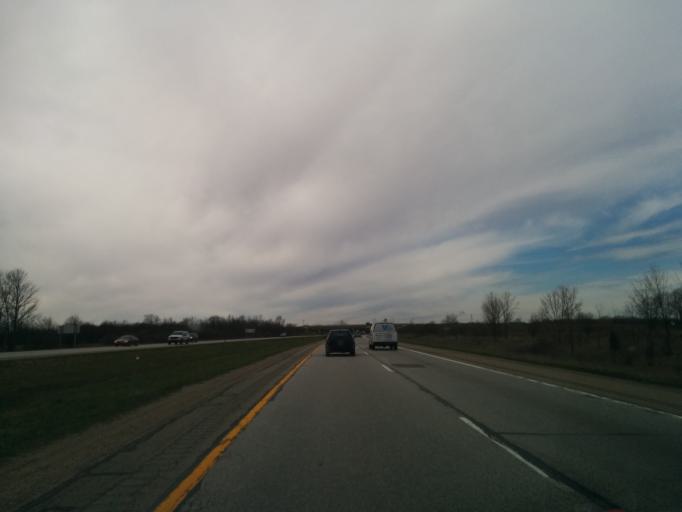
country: US
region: Michigan
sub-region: Ottawa County
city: Jenison
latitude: 42.8683
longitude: -85.7968
